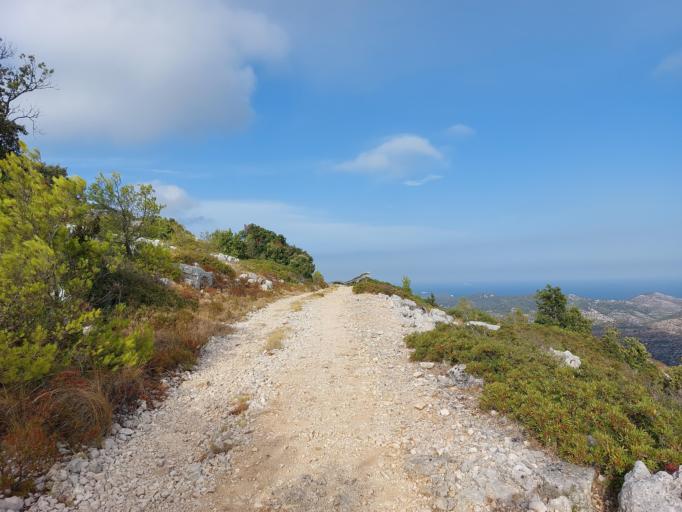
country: HR
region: Dubrovacko-Neretvanska
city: Smokvica
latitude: 42.7495
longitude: 16.8600
